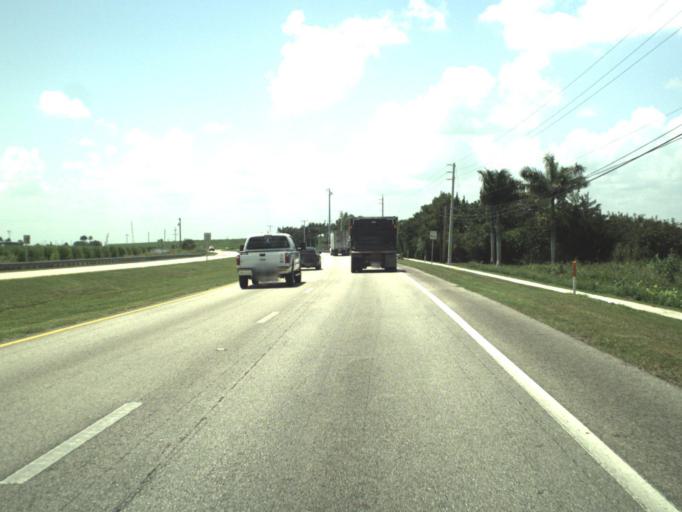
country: US
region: Florida
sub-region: Palm Beach County
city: South Bay
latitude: 26.6788
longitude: -80.7276
